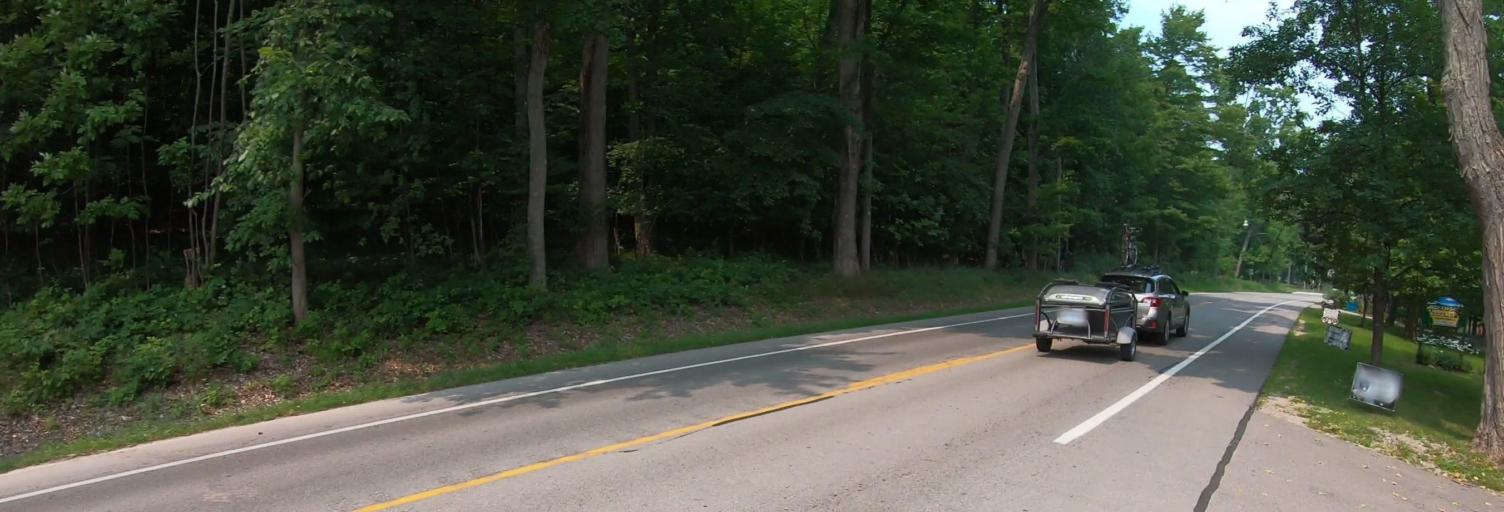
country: US
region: Michigan
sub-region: Leelanau County
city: Leland
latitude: 45.1229
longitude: -85.6178
